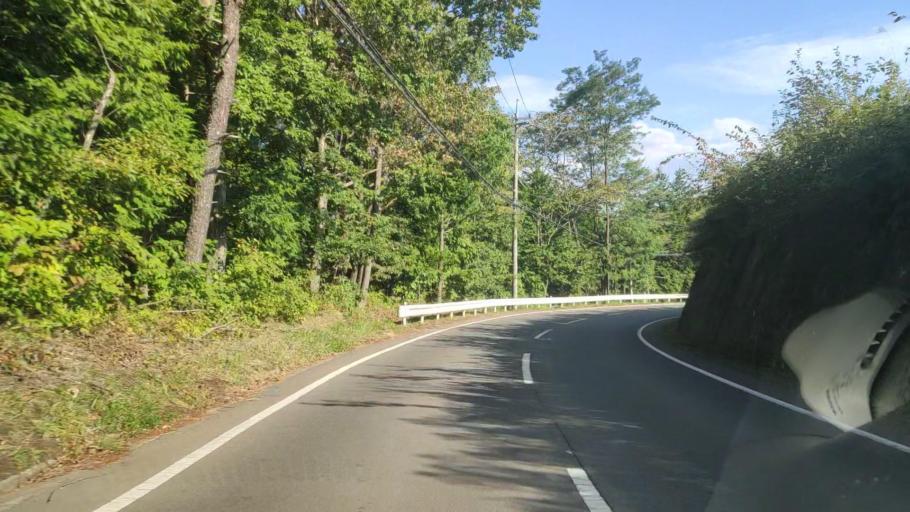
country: JP
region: Nagano
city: Suzaka
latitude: 36.5601
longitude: 138.5590
